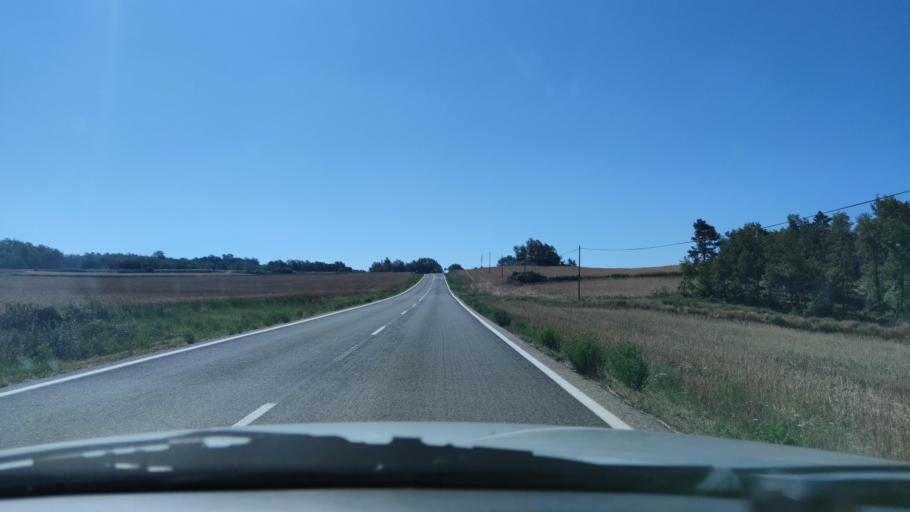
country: ES
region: Catalonia
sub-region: Provincia de Lleida
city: Solsona
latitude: 41.8979
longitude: 1.5392
